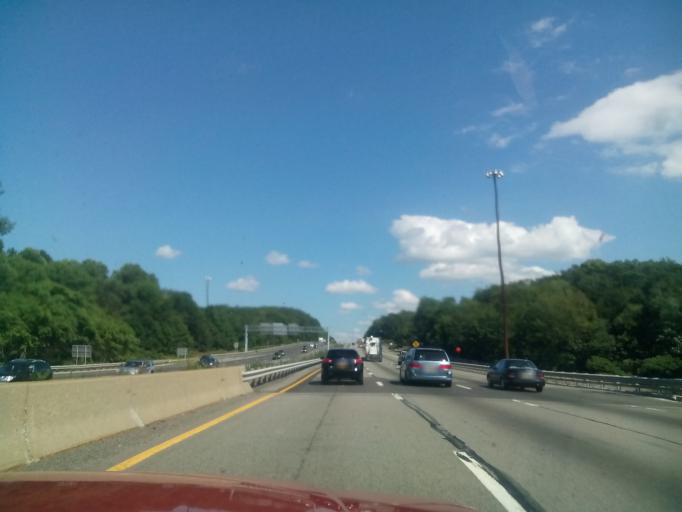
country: US
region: New Jersey
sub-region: Morris County
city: Netcong
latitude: 40.8904
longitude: -74.6972
